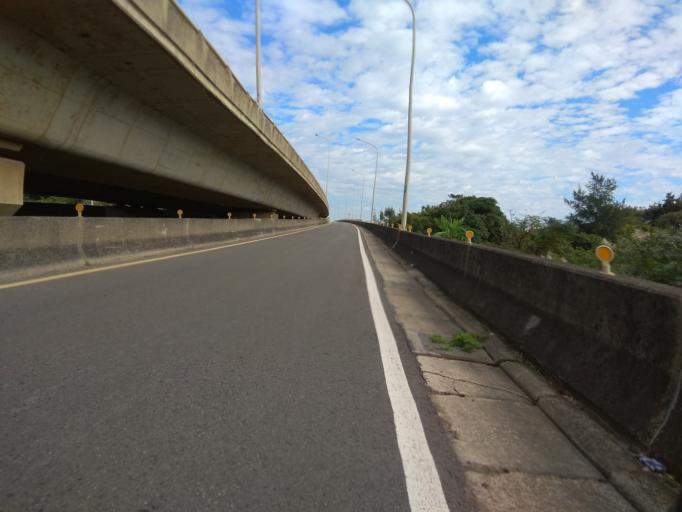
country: TW
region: Taiwan
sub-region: Hsinchu
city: Zhubei
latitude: 25.0417
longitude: 121.0749
